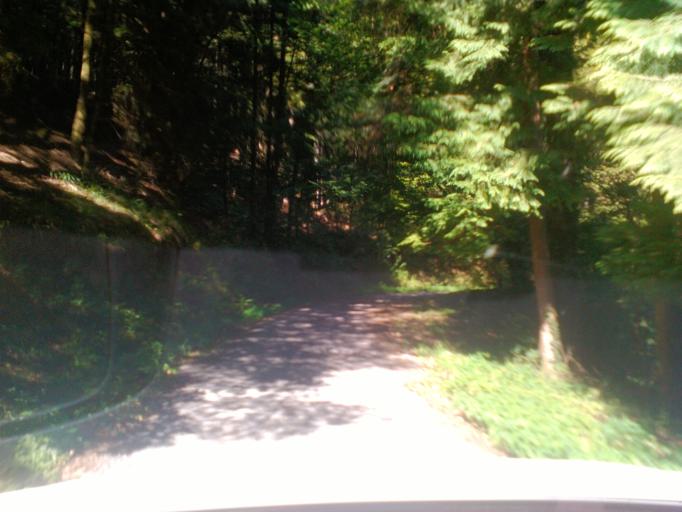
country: FR
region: Lorraine
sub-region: Departement des Vosges
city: Senones
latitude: 48.4057
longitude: 6.9765
